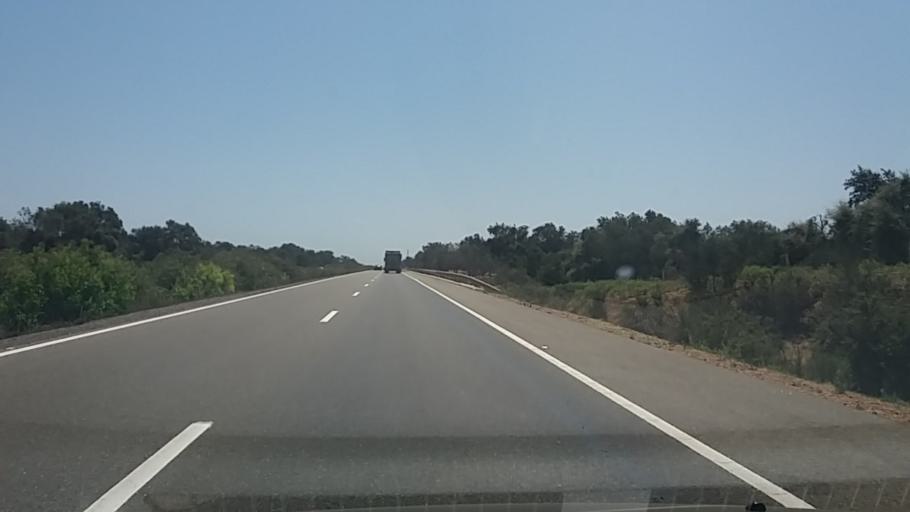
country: MA
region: Gharb-Chrarda-Beni Hssen
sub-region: Kenitra Province
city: Kenitra
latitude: 34.1515
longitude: -6.6788
